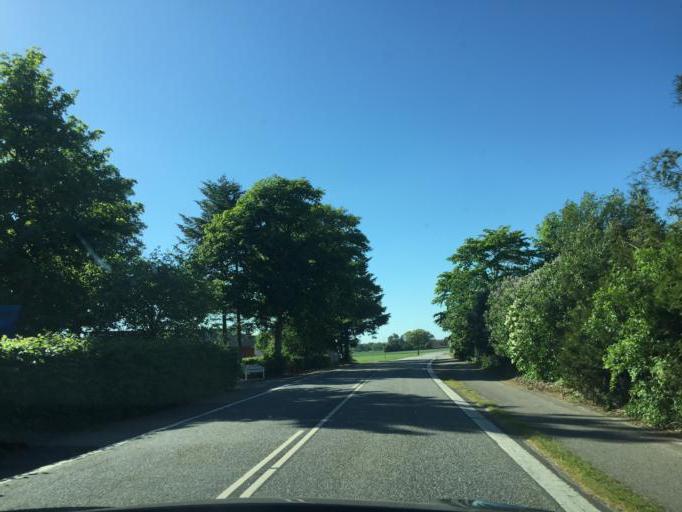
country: DK
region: Zealand
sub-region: Koge Kommune
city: Borup
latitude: 55.4333
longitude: 11.9738
